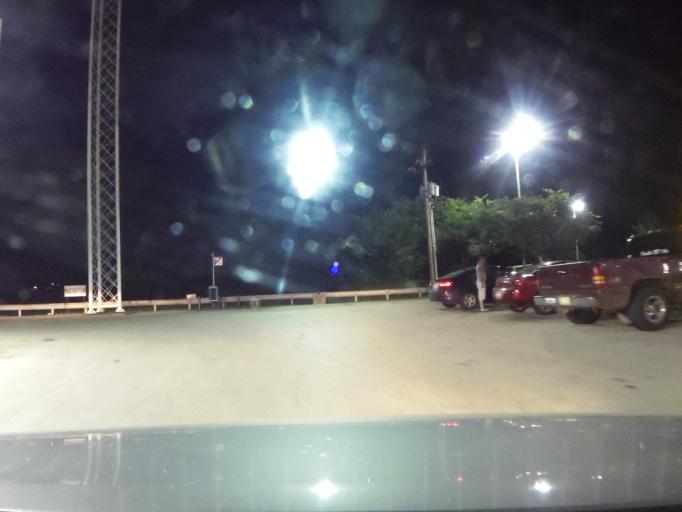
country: US
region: Kentucky
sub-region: Trigg County
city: Cadiz
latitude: 36.8803
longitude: -87.7385
